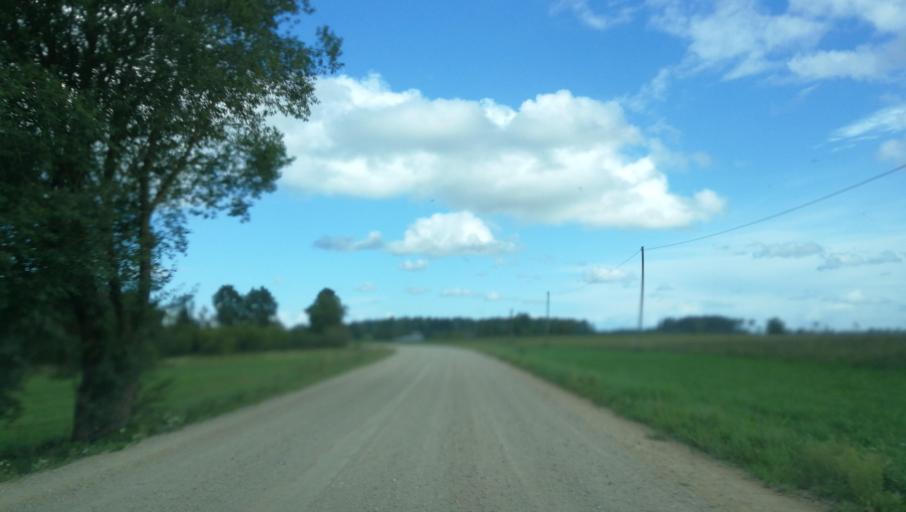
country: LV
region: Malpils
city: Malpils
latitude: 56.9613
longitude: 24.9375
